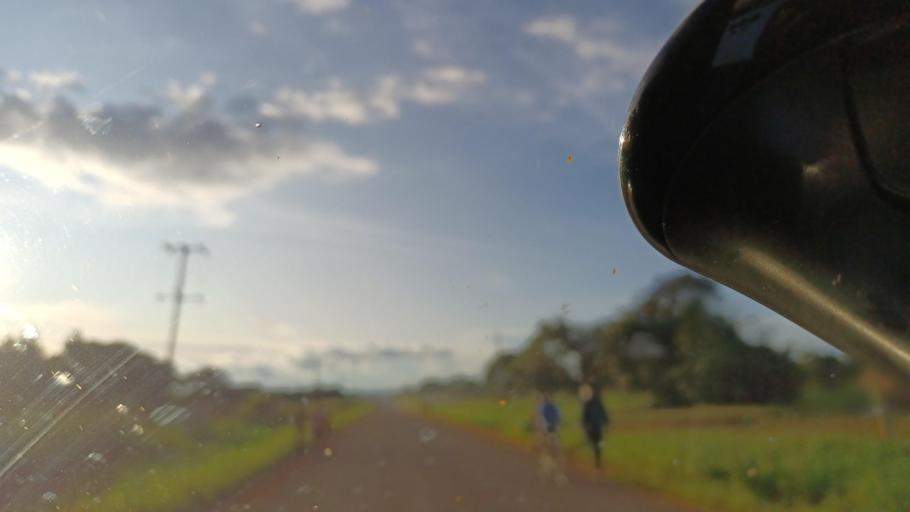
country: ZM
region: North-Western
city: Kasempa
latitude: -13.4649
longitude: 25.8563
